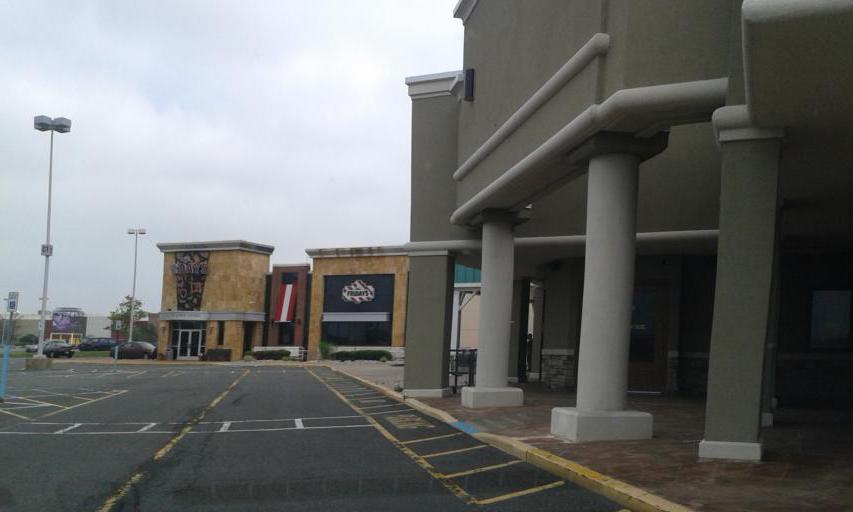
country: US
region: New York
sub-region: Richmond County
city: Staten Island
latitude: 40.5783
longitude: -74.1644
